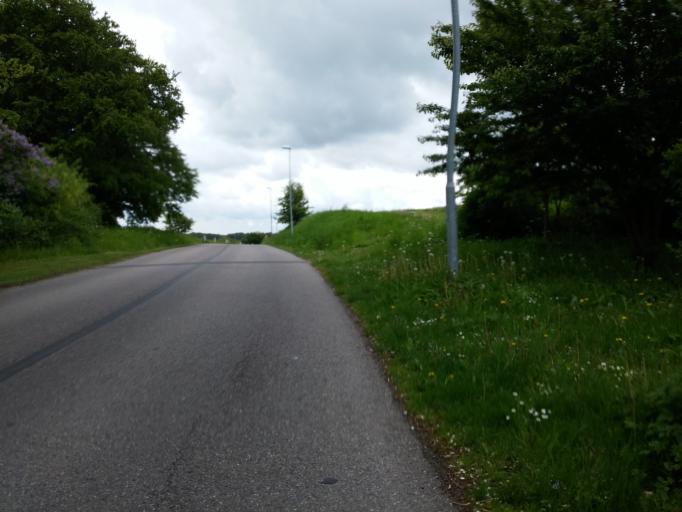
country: DK
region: South Denmark
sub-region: Kerteminde Kommune
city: Munkebo
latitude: 55.4404
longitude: 10.5419
